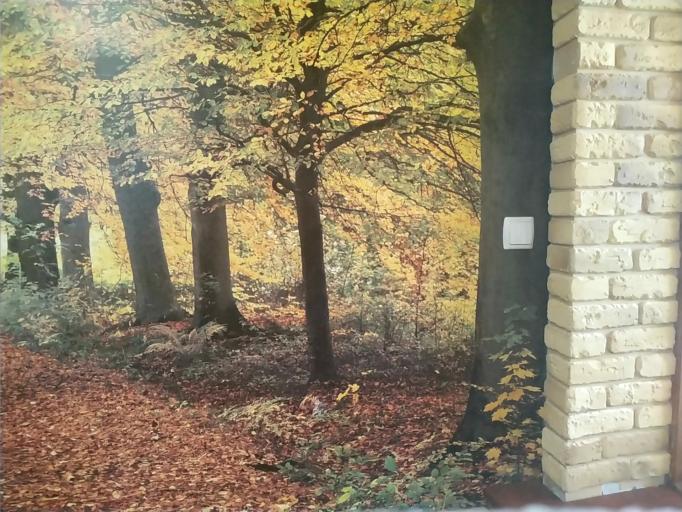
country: RU
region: Tverskaya
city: Vyshniy Volochek
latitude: 57.6267
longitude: 34.5787
